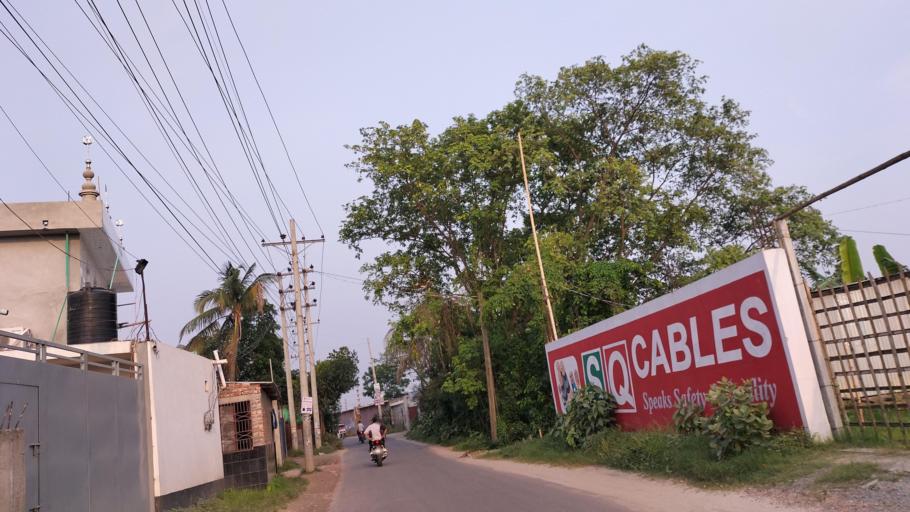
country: BD
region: Dhaka
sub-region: Dhaka
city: Dhaka
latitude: 23.6527
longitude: 90.3486
